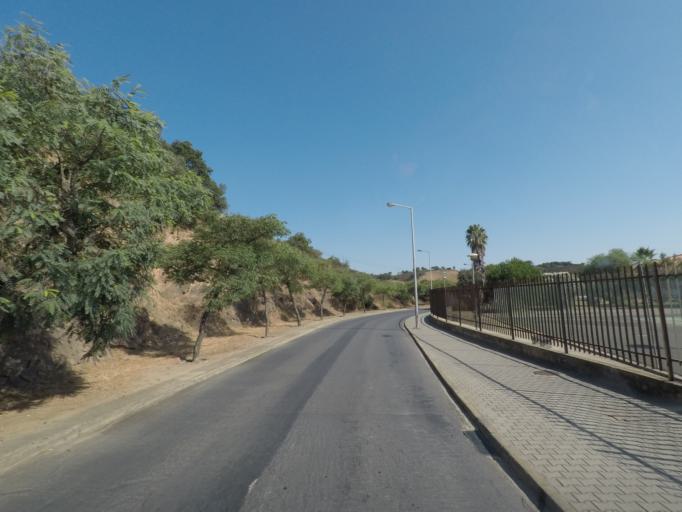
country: PT
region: Beja
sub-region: Odemira
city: Odemira
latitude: 37.5981
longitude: -8.6340
